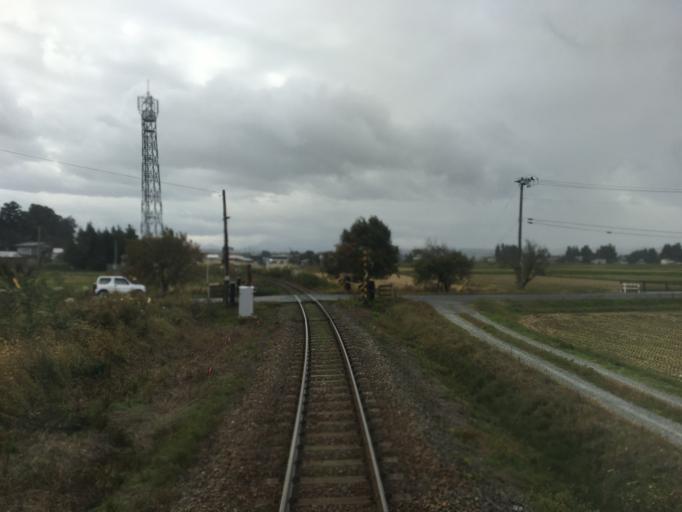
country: JP
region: Yamagata
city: Nagai
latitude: 38.0744
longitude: 140.0290
